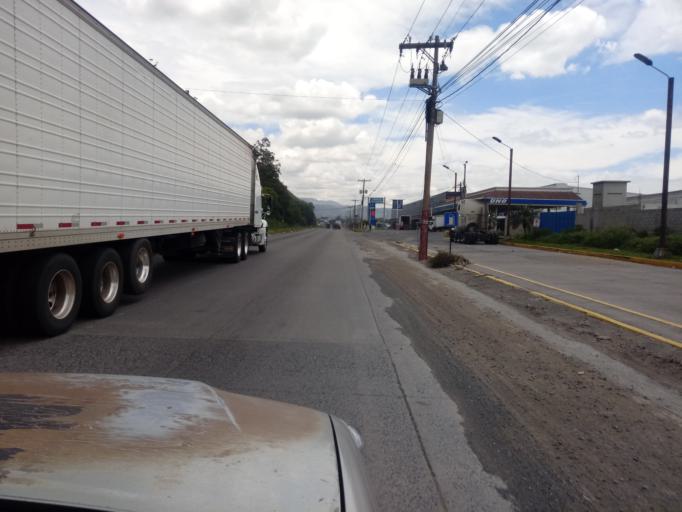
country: GT
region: Escuintla
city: San Vicente Pacaya
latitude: 14.4506
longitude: -90.6438
